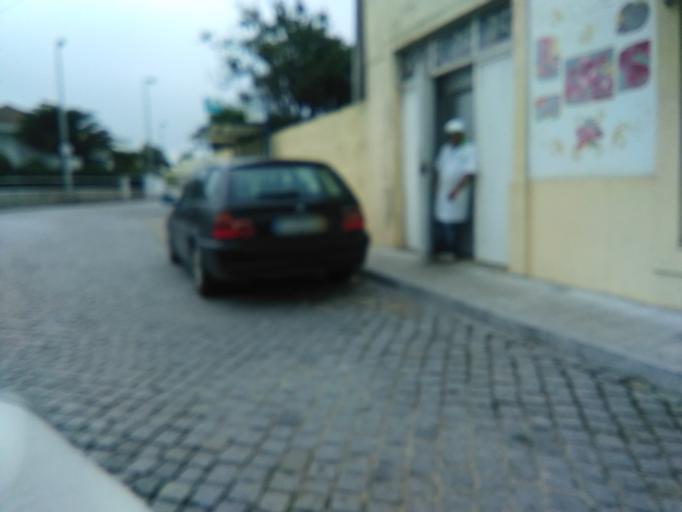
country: PT
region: Porto
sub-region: Matosinhos
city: Santa Cruz do Bispo
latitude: 41.2247
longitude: -8.7034
